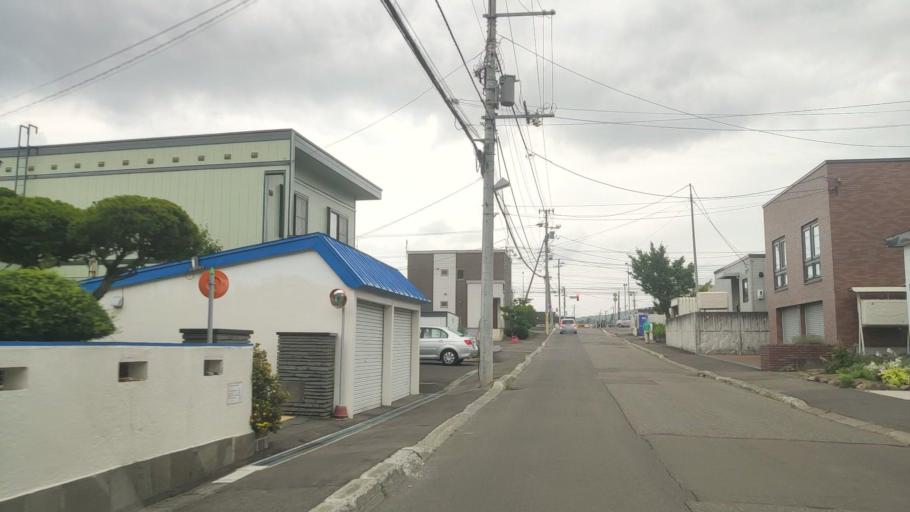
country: JP
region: Hokkaido
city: Sapporo
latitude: 42.9628
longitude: 141.3185
